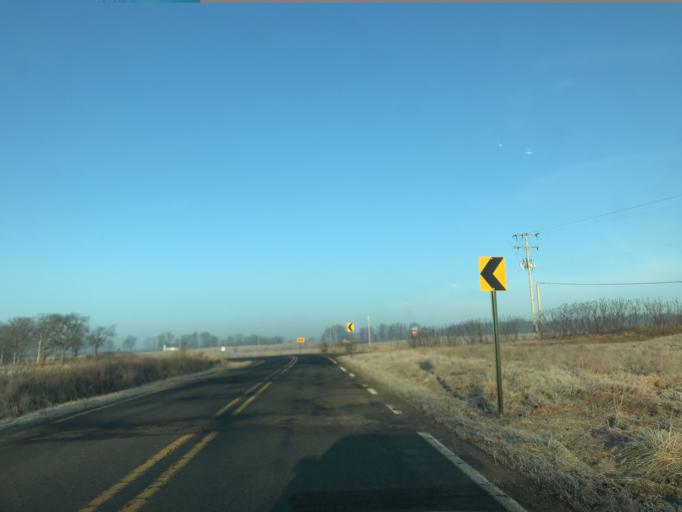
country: US
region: Michigan
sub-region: Ingham County
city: Leslie
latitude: 42.4214
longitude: -84.5169
